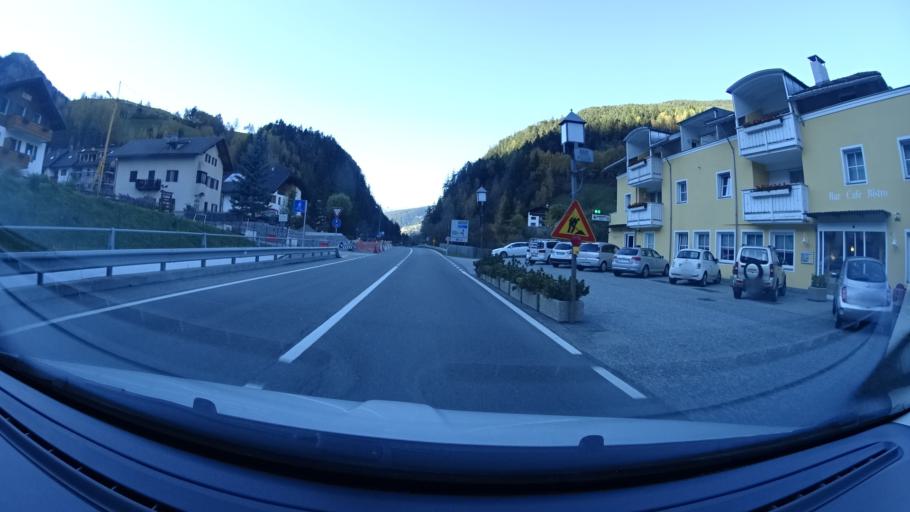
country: IT
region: Trentino-Alto Adige
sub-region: Bolzano
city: Ortisei
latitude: 46.5743
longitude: 11.6464
